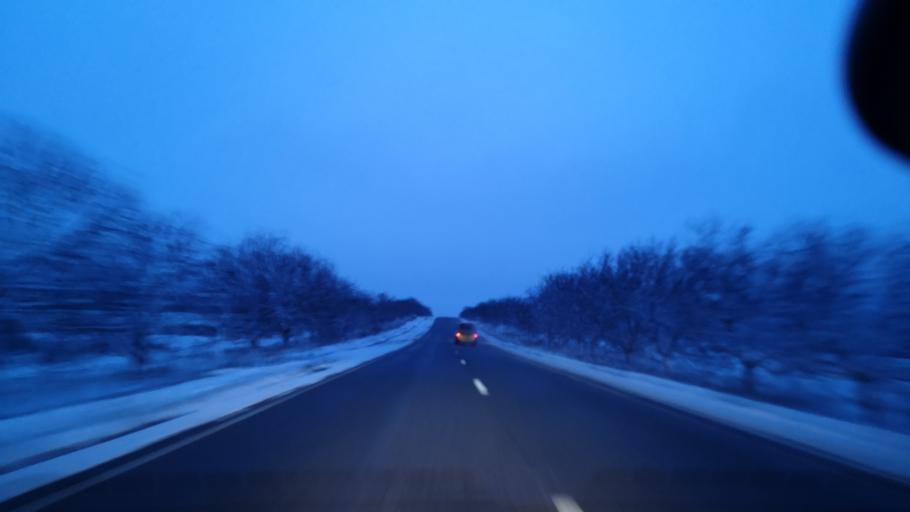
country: MD
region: Rezina
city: Saharna
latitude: 47.6208
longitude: 28.8332
